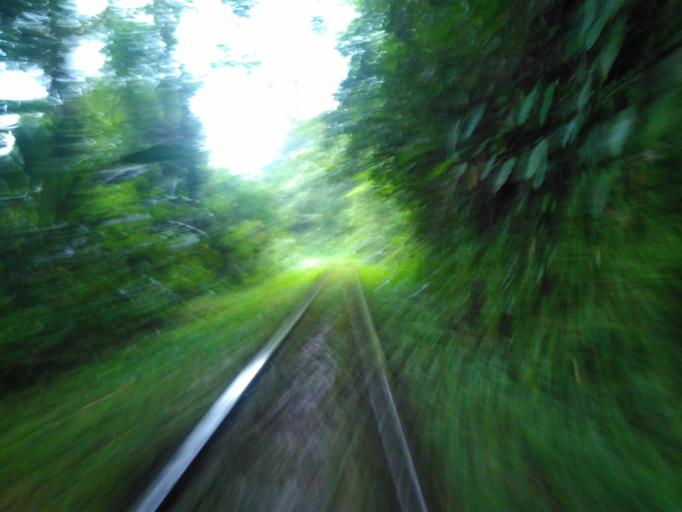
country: CO
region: Valle del Cauca
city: Buenaventura
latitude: 3.8433
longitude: -76.8764
